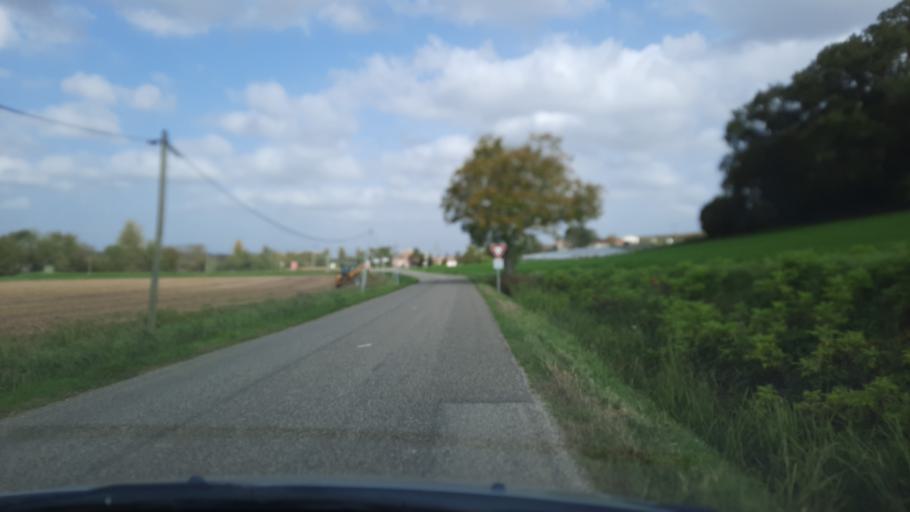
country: FR
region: Midi-Pyrenees
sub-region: Departement du Tarn-et-Garonne
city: Lafrancaise
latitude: 44.1862
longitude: 1.2858
